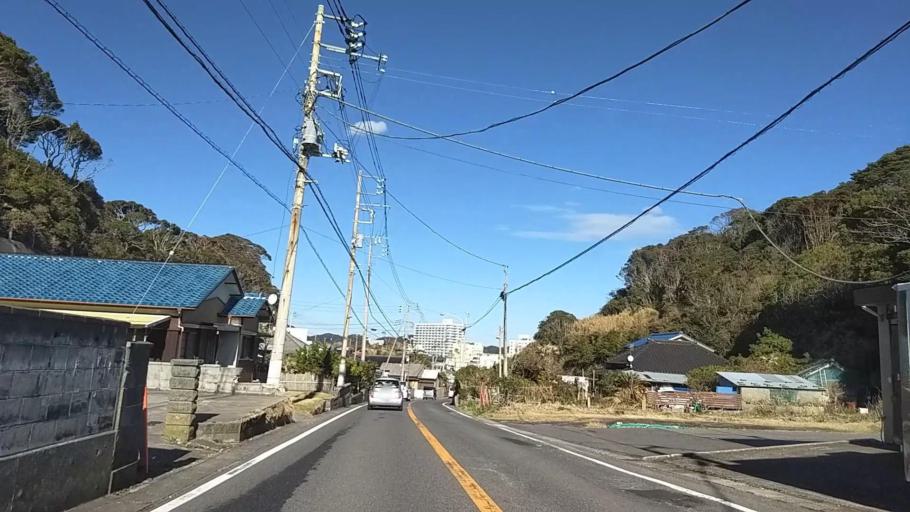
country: JP
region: Chiba
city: Katsuura
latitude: 35.1764
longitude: 140.3466
